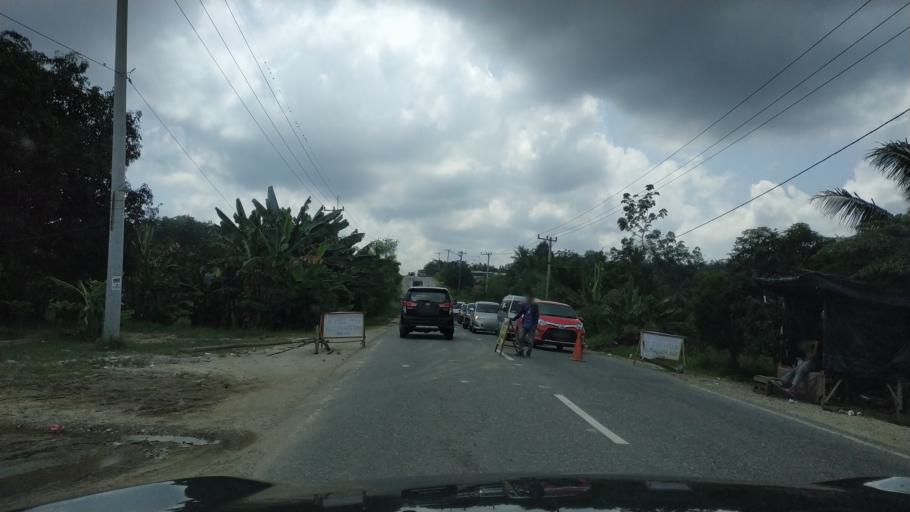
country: ID
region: Riau
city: Pangkalanbunut
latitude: 0.3036
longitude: 101.9121
